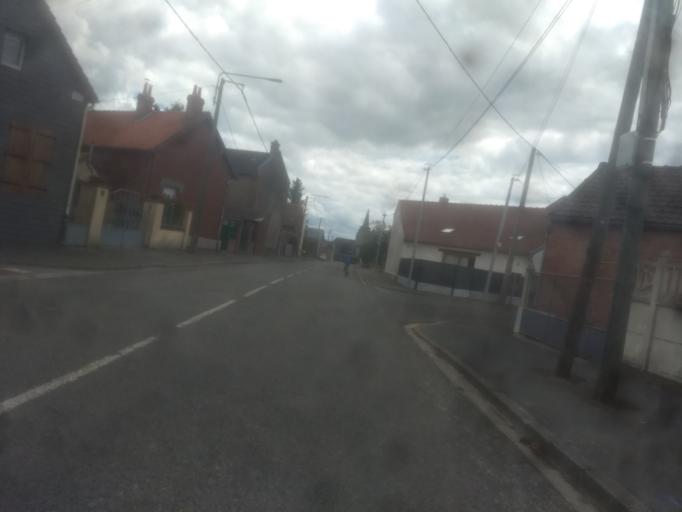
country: FR
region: Nord-Pas-de-Calais
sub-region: Departement du Pas-de-Calais
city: Agny
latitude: 50.2118
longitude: 2.7783
